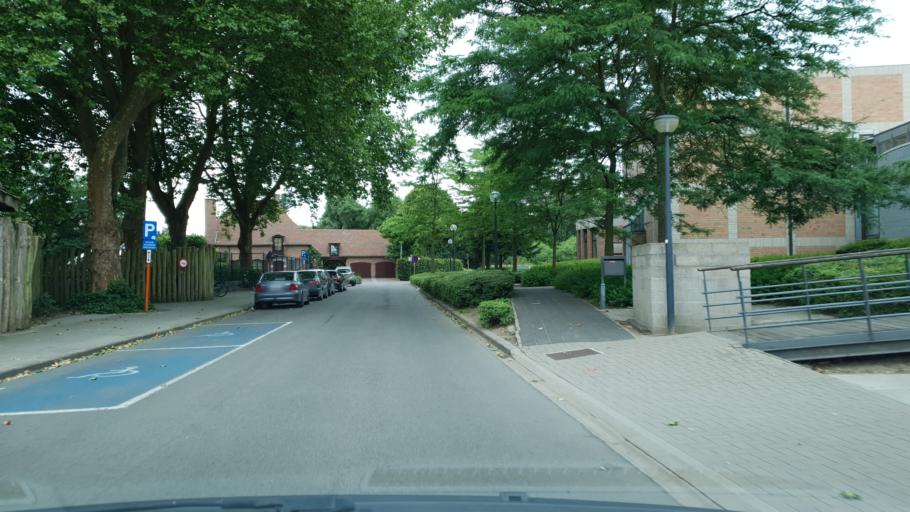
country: BE
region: Flanders
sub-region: Provincie Antwerpen
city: Geel
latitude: 51.1606
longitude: 4.9860
